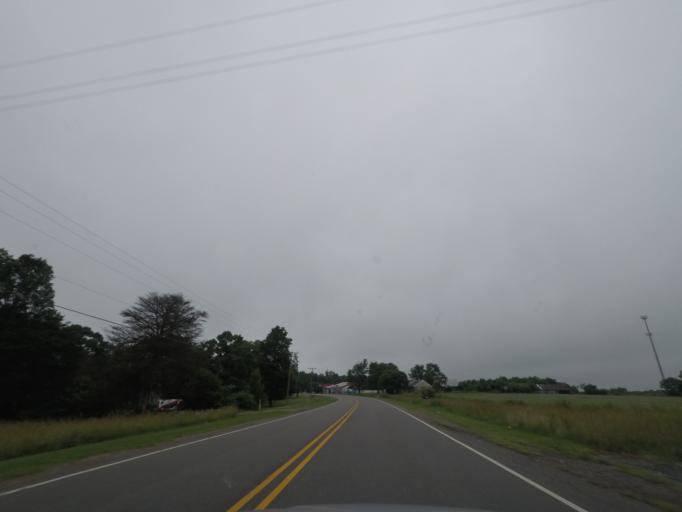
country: US
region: Virginia
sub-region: Fluvanna County
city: Weber City
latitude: 37.6276
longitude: -78.3660
